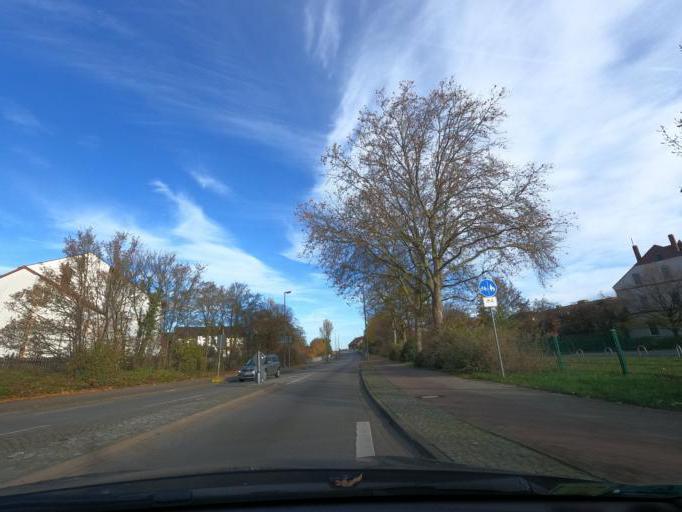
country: DE
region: Lower Saxony
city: Peine
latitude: 52.3150
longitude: 10.2328
